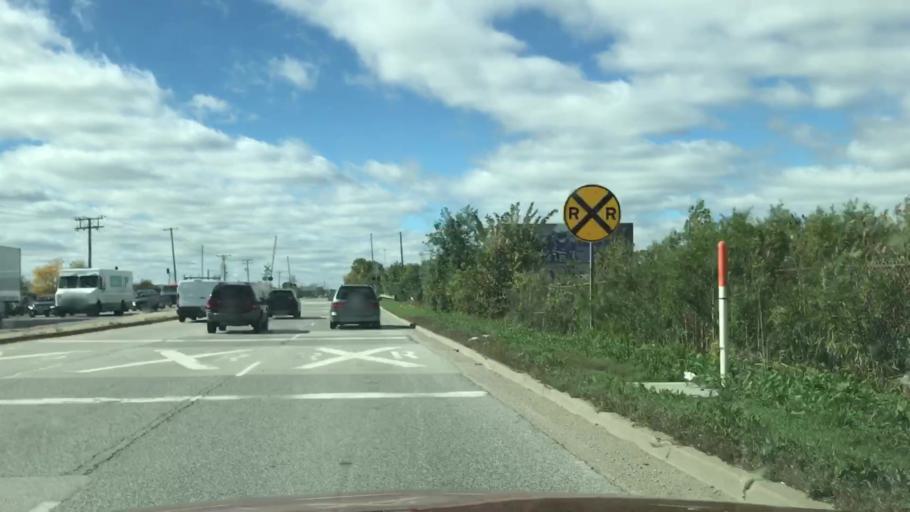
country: US
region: Illinois
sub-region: Cook County
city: Rosemont
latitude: 42.0085
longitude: -87.9231
